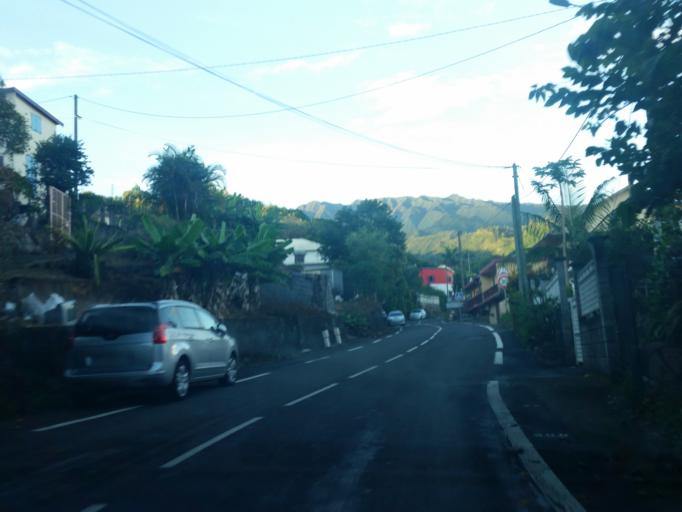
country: RE
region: Reunion
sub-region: Reunion
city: L'Entre-Deux
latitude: -21.2428
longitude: 55.4806
